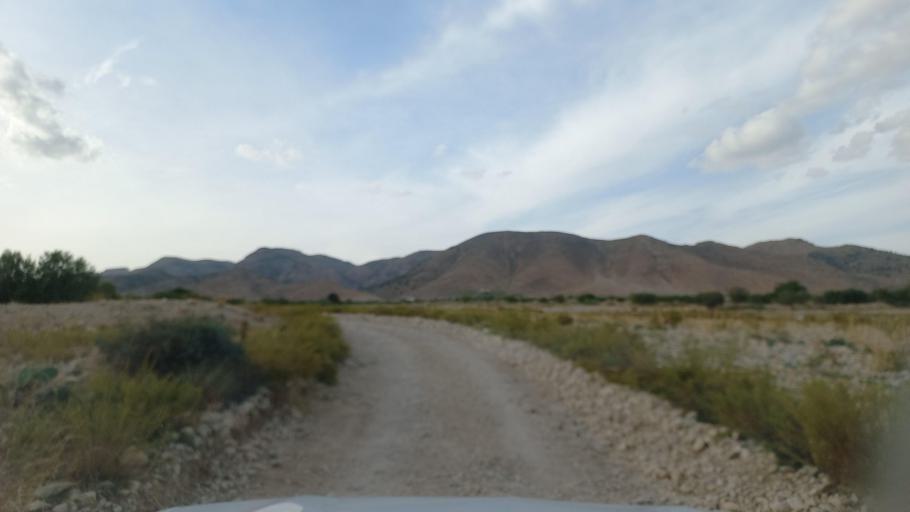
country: TN
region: Al Qasrayn
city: Sbiba
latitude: 35.4445
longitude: 9.0707
